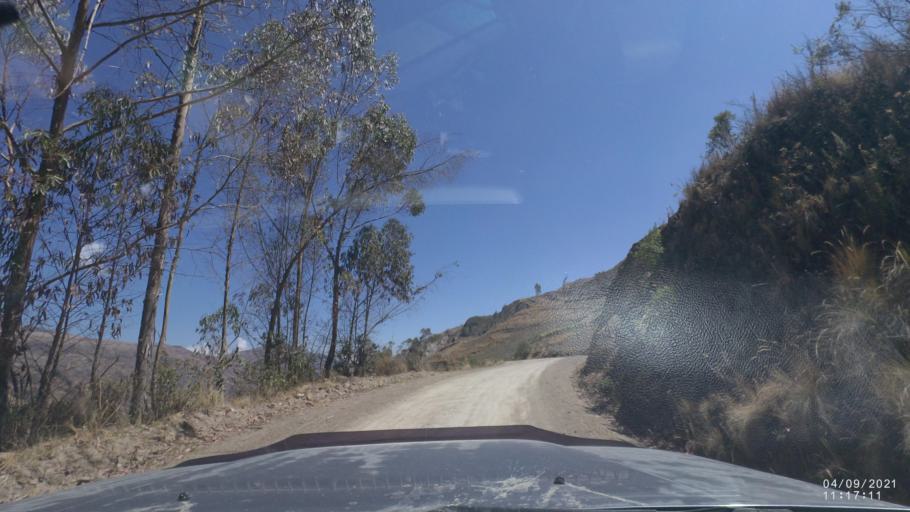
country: BO
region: Cochabamba
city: Sipe Sipe
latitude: -17.2701
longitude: -66.4862
